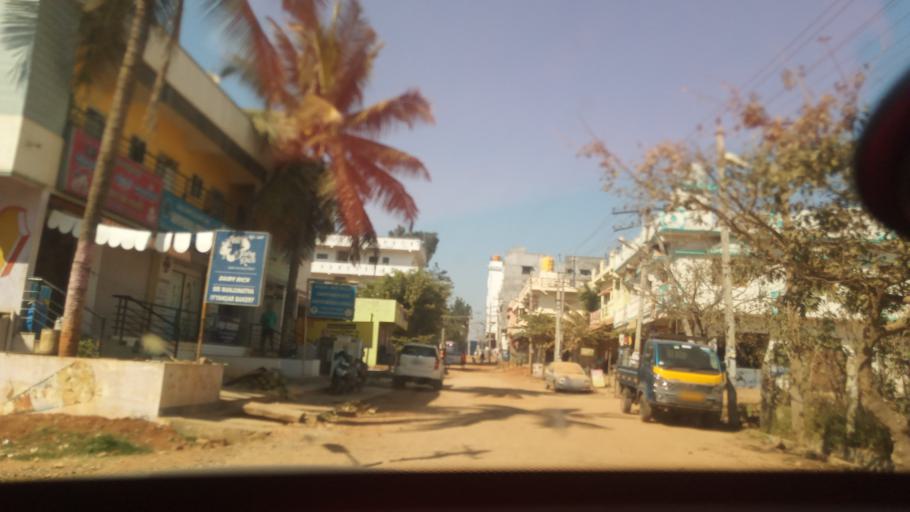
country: IN
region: Karnataka
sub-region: Bangalore Rural
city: Nelamangala
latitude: 13.0390
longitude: 77.4940
